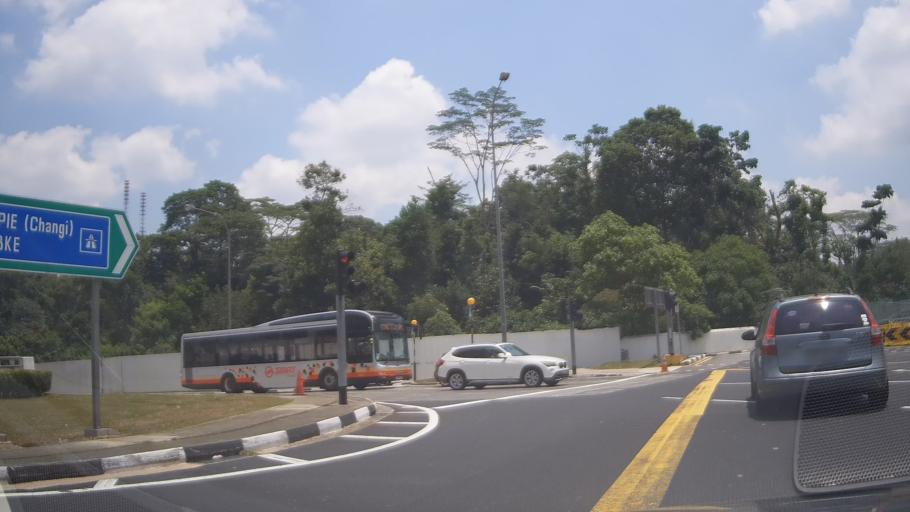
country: SG
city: Singapore
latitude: 1.3419
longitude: 103.7777
